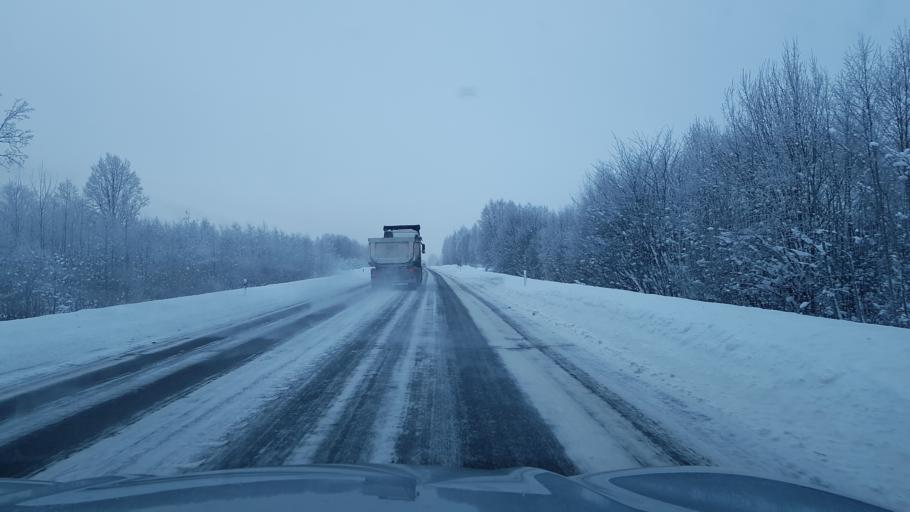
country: EE
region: Ida-Virumaa
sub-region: Johvi vald
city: Johvi
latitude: 59.2180
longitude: 27.3383
